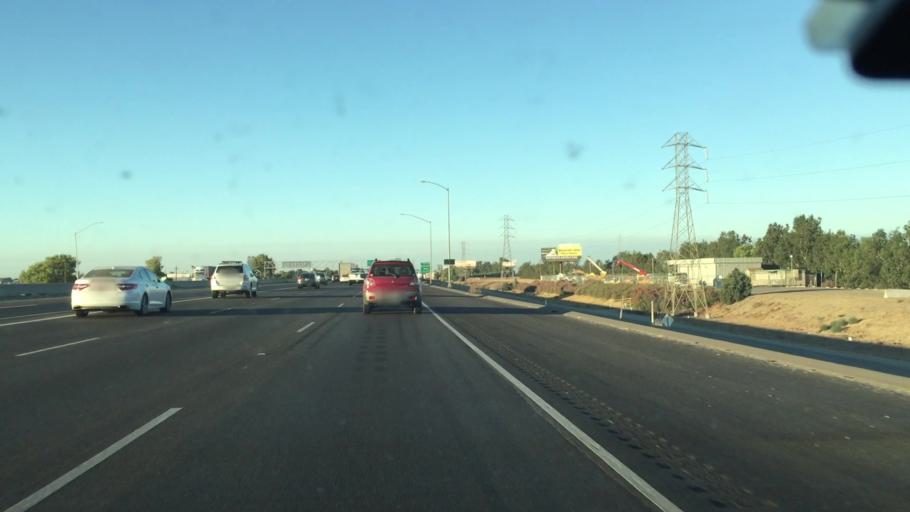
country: US
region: California
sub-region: San Joaquin County
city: Lathrop
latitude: 37.7748
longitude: -121.3207
